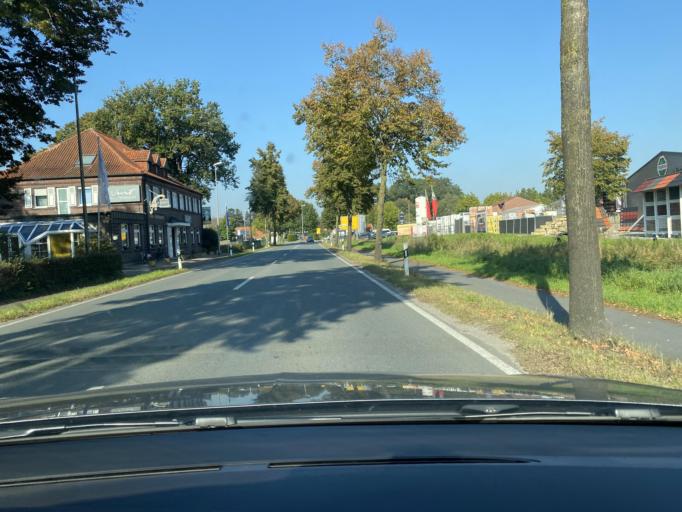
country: DE
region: North Rhine-Westphalia
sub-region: Regierungsbezirk Munster
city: Gronau
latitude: 52.1897
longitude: 7.0299
